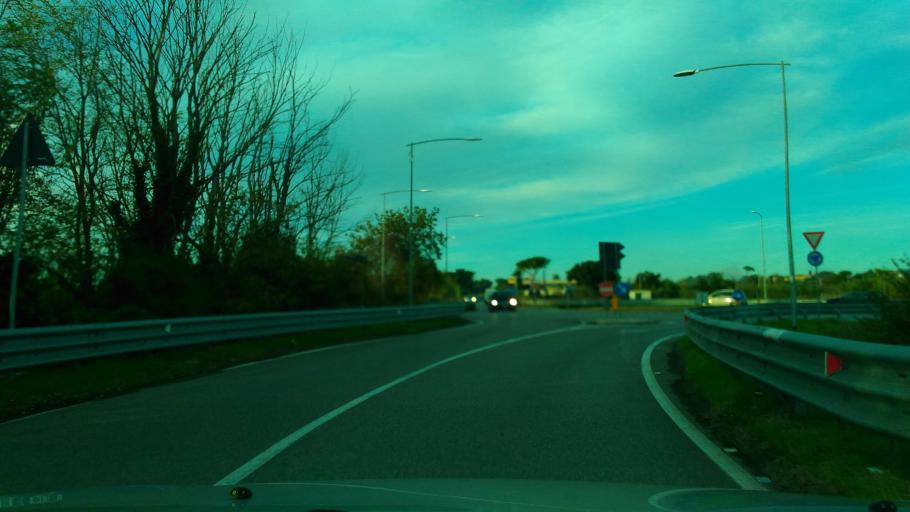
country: IT
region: Tuscany
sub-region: Provincia di Livorno
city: S.P. in Palazzi
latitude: 43.3313
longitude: 10.5064
